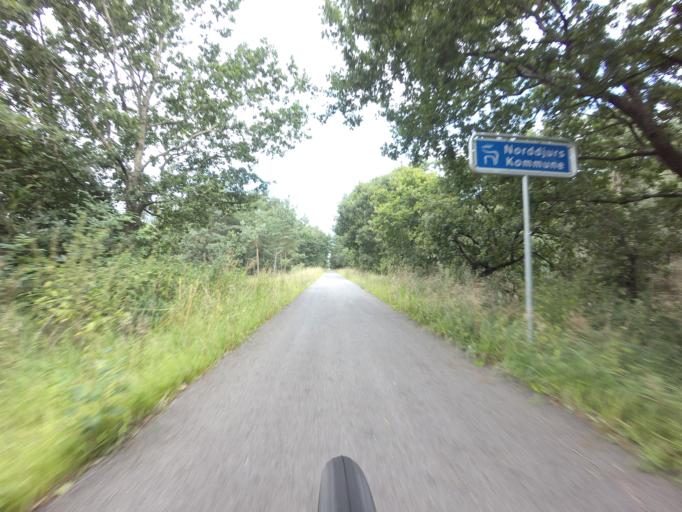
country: DK
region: Central Jutland
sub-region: Norddjurs Kommune
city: Auning
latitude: 56.4038
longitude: 10.4000
